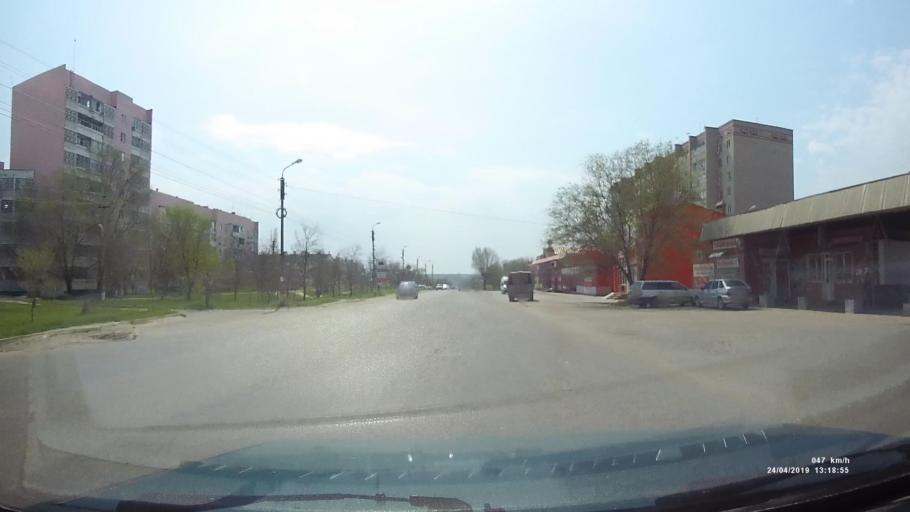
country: RU
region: Kalmykiya
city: Elista
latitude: 46.3024
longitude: 44.2940
